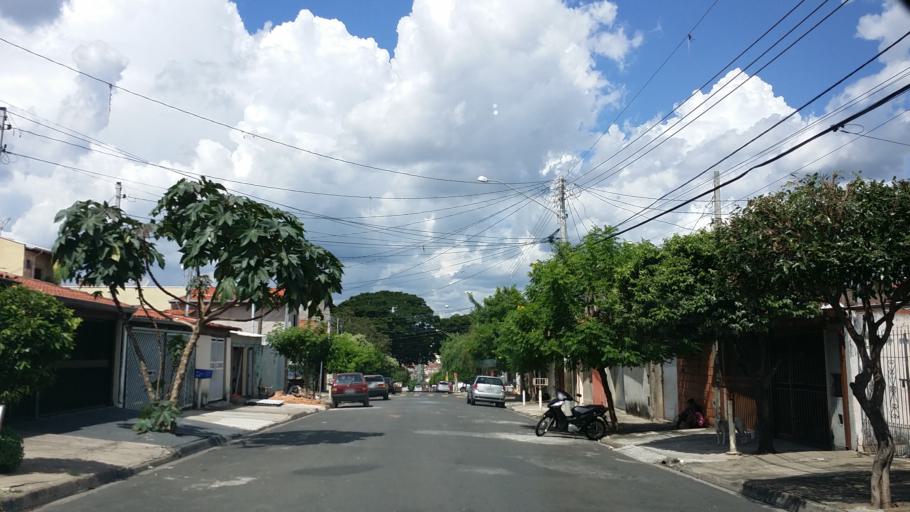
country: BR
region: Sao Paulo
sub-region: Indaiatuba
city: Indaiatuba
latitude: -23.1171
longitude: -47.2405
